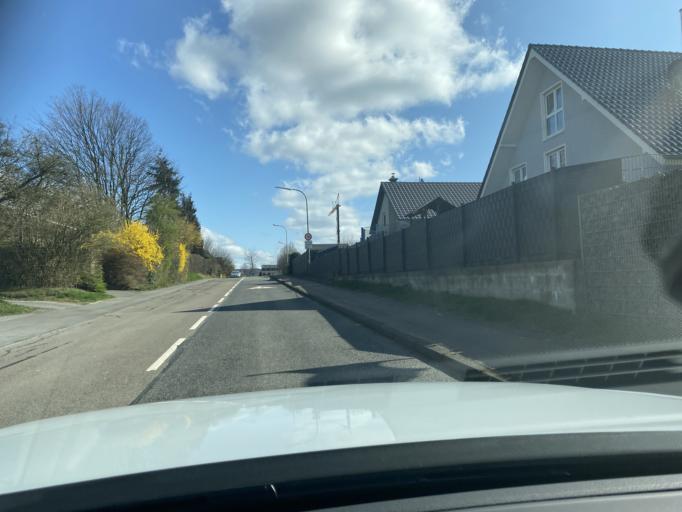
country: DE
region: North Rhine-Westphalia
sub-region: Regierungsbezirk Koln
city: Lindlar
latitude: 51.0173
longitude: 7.3588
